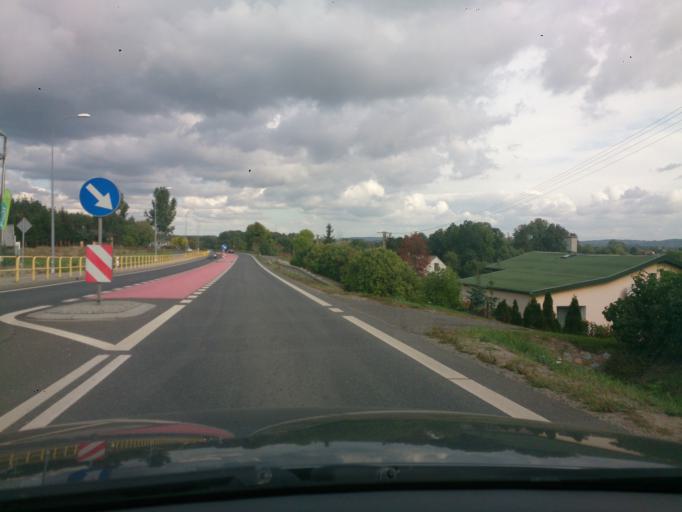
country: PL
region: Kujawsko-Pomorskie
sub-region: Grudziadz
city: Grudziadz
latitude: 53.4888
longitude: 18.6764
